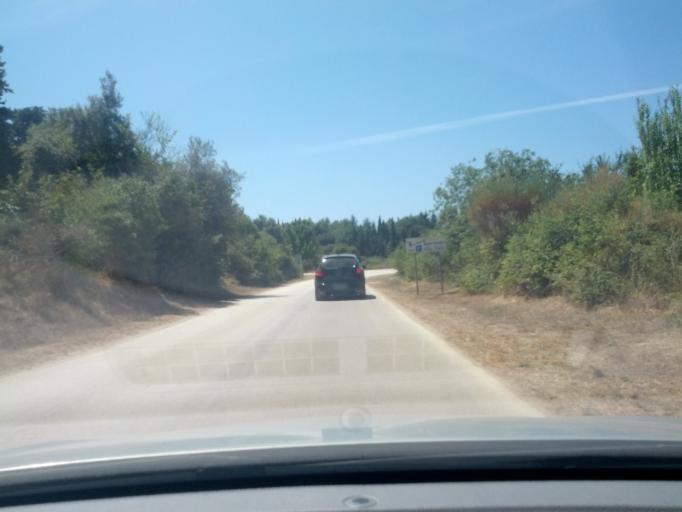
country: HR
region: Istarska
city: Fazana
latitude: 44.8991
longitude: 13.8104
